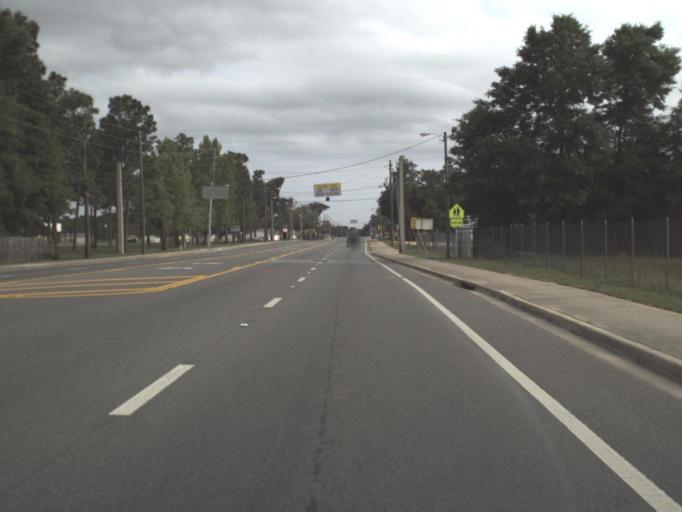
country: US
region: Florida
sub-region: Santa Rosa County
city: Milton
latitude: 30.6522
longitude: -87.0460
